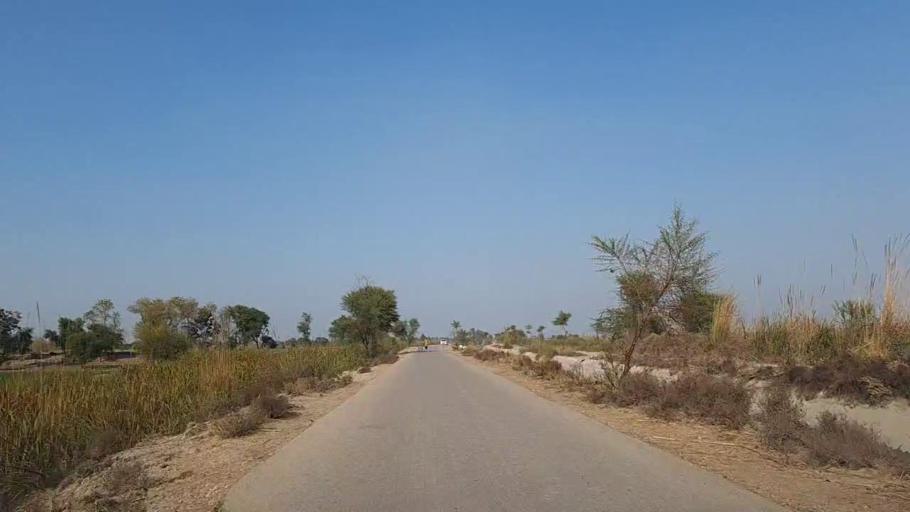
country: PK
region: Sindh
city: Daur
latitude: 26.4212
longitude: 68.2606
